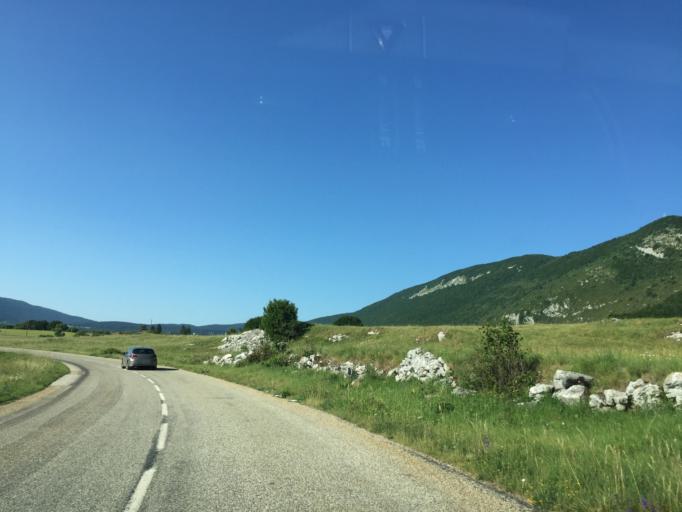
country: FR
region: Rhone-Alpes
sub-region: Departement de la Drome
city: Saint-Laurent-en-Royans
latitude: 44.9091
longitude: 5.3735
